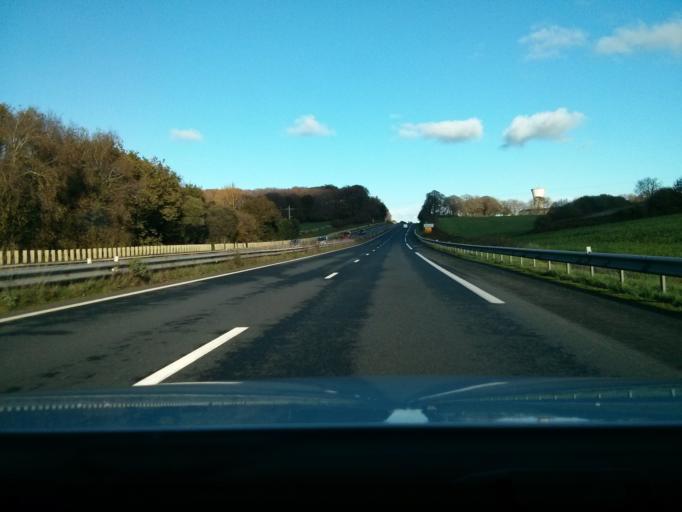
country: FR
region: Brittany
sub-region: Departement du Finistere
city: Morlaix
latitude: 48.5614
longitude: -3.8659
